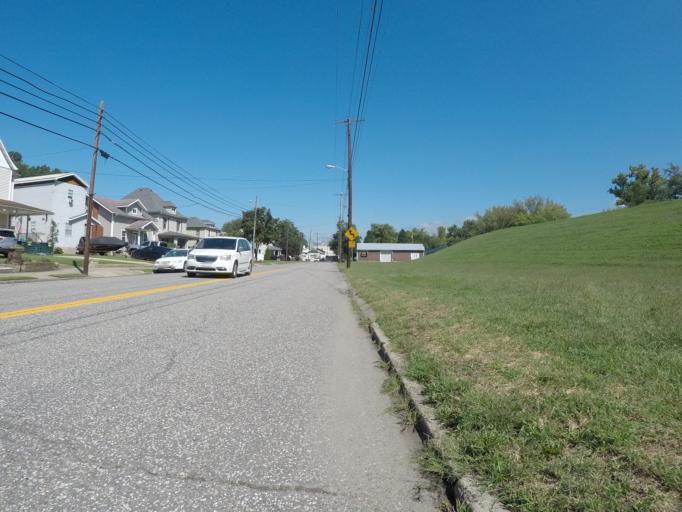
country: US
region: Kentucky
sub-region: Boyd County
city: Catlettsburg
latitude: 38.4117
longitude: -82.5981
